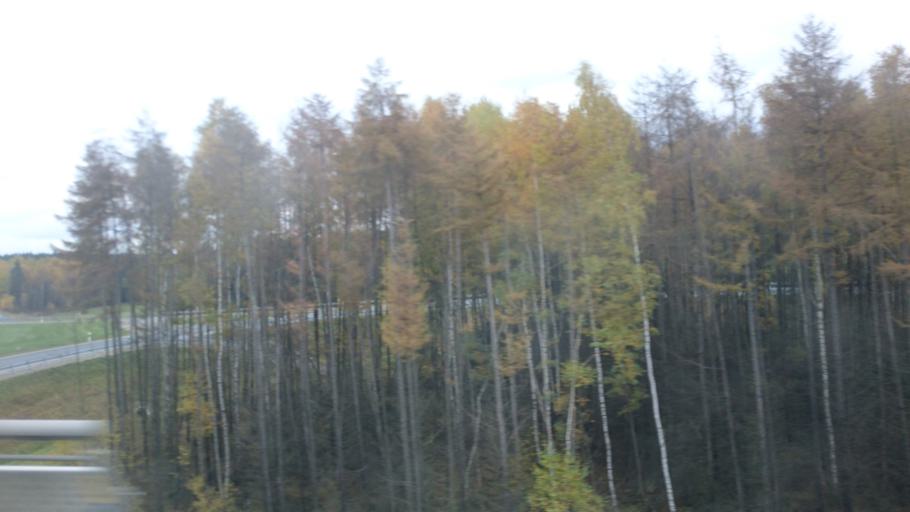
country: DE
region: Thuringia
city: Dittersdorf
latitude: 50.6567
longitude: 11.8140
